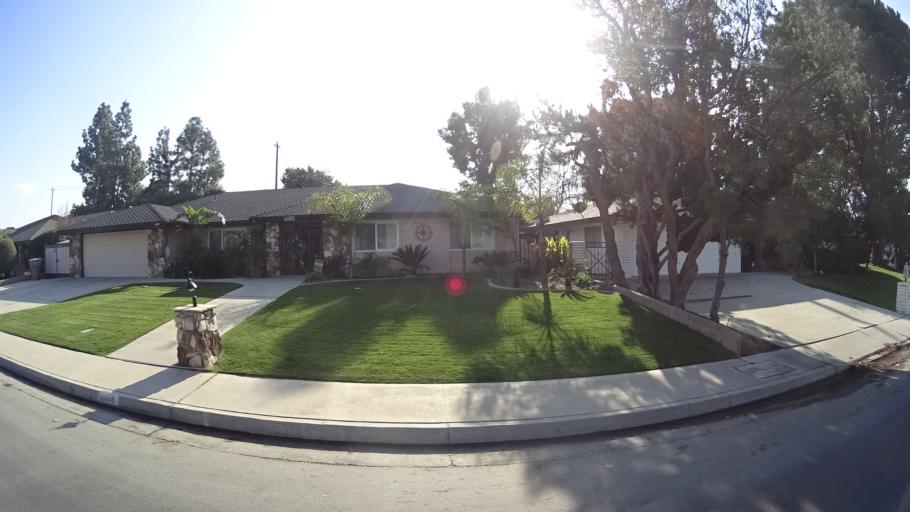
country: US
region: California
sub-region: Kern County
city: Oildale
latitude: 35.4123
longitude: -118.9580
